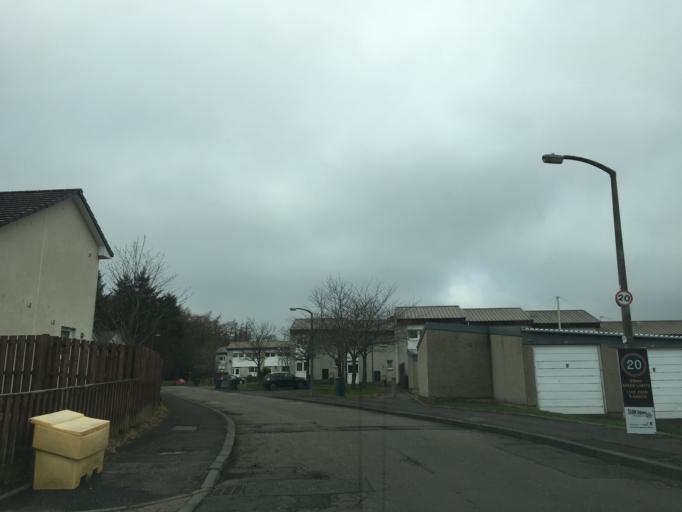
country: GB
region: Scotland
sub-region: Edinburgh
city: Colinton
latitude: 55.9027
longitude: -3.2257
